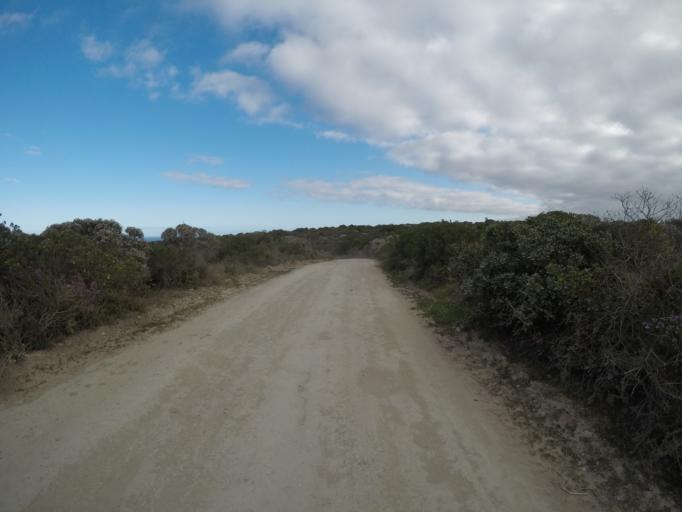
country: ZA
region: Western Cape
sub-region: Eden District Municipality
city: Riversdale
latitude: -34.4234
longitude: 21.3304
